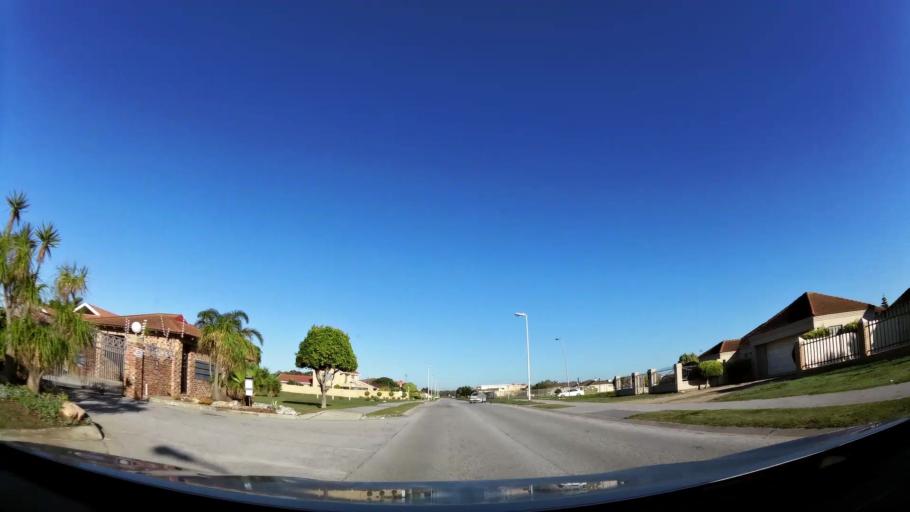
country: ZA
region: Eastern Cape
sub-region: Nelson Mandela Bay Metropolitan Municipality
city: Port Elizabeth
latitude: -34.0020
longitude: 25.6562
